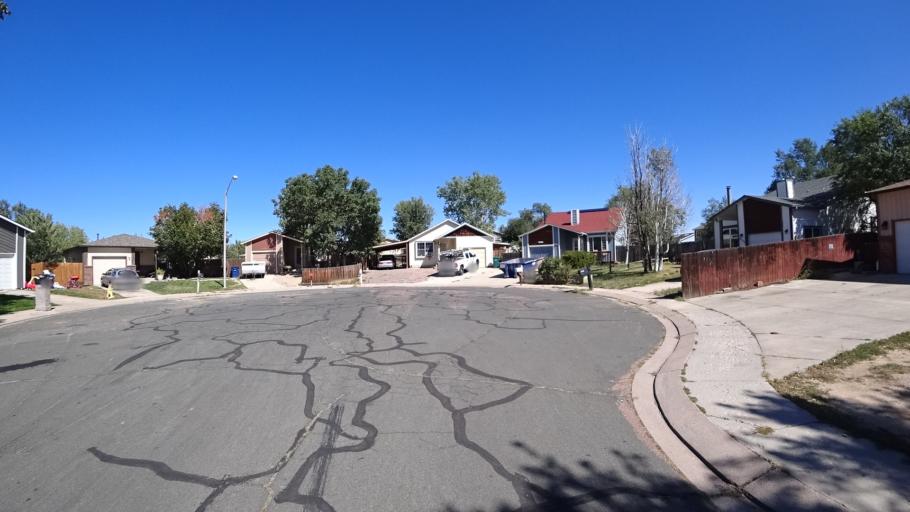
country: US
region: Colorado
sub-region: El Paso County
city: Stratmoor
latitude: 38.7842
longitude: -104.7436
